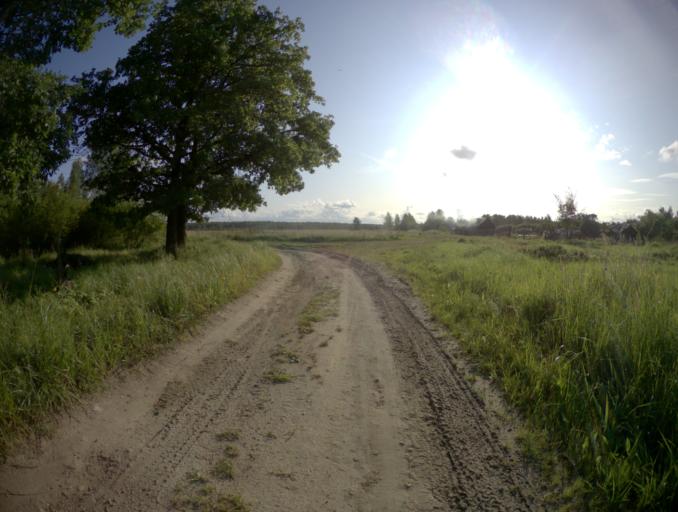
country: RU
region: Vladimir
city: Raduzhnyy
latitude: 56.0903
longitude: 40.2692
